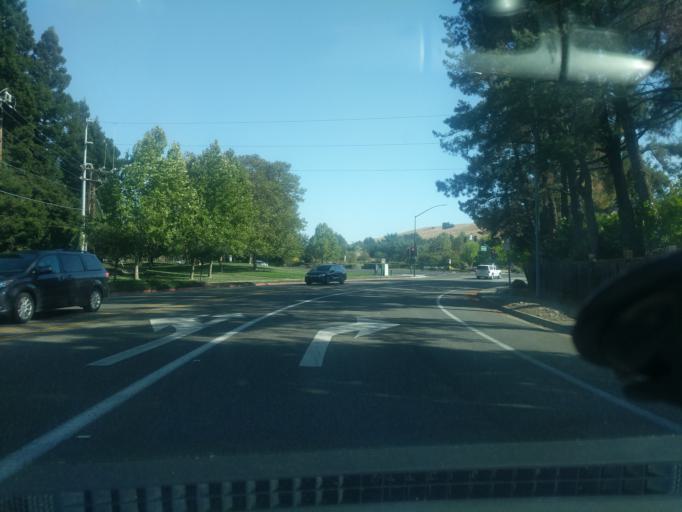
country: US
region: California
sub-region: Contra Costa County
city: Diablo
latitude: 37.8167
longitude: -121.9690
